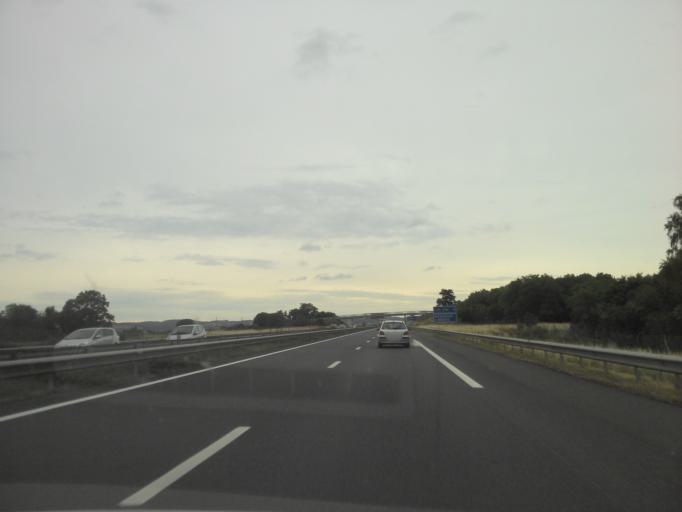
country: FR
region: Auvergne
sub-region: Departement du Puy-de-Dome
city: Saint-Bonnet-pres-Riom
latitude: 45.9286
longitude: 3.1375
